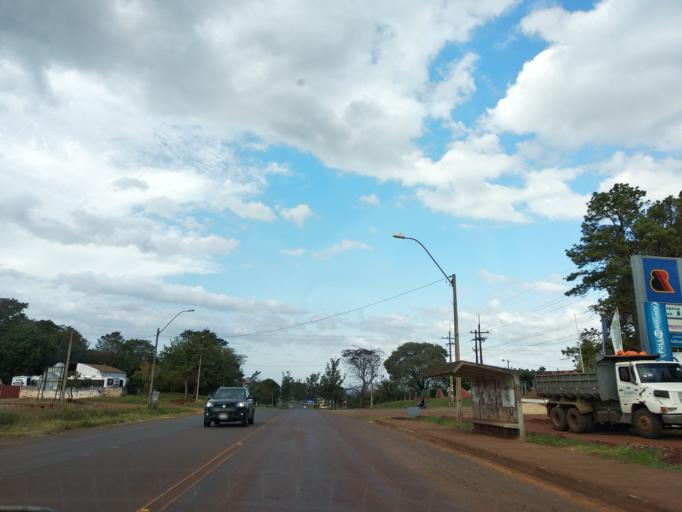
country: PY
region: Itapua
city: San Juan del Parana
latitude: -27.2889
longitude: -55.9370
